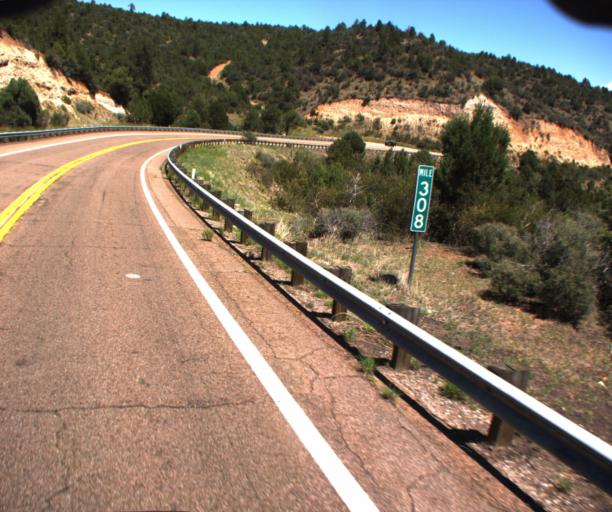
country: US
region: Arizona
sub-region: Navajo County
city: Cibecue
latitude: 33.9279
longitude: -110.3585
